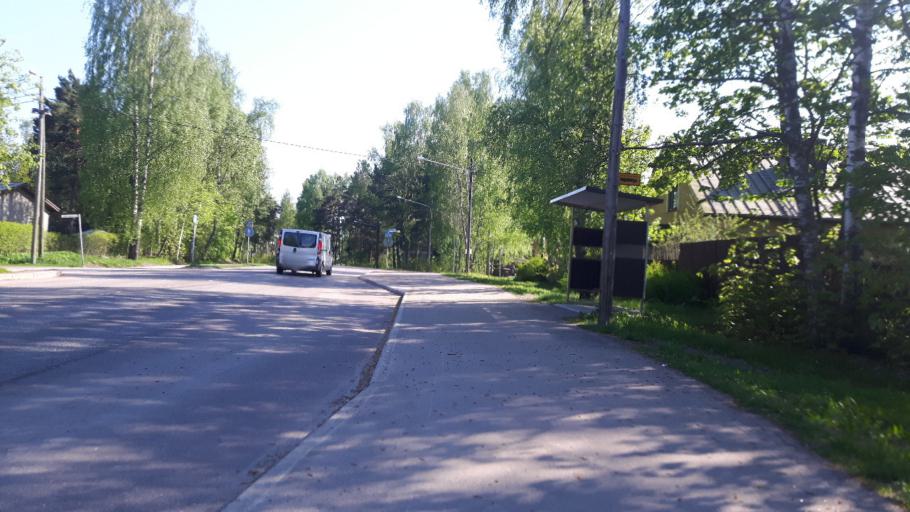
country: FI
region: Kymenlaakso
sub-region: Kotka-Hamina
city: Kotka
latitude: 60.4795
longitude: 26.8667
